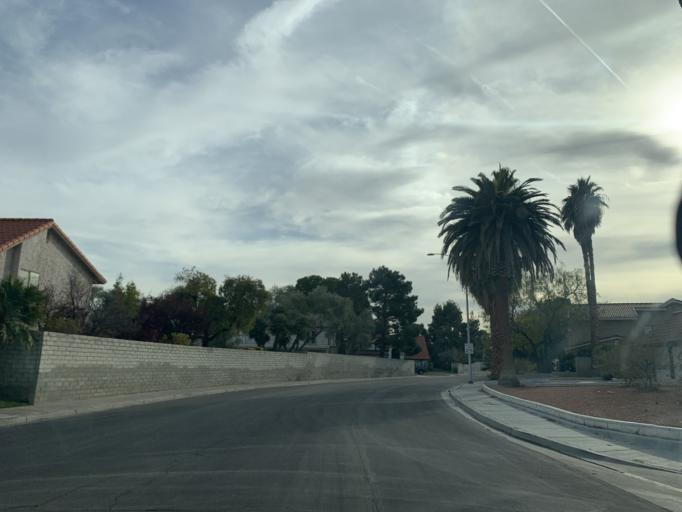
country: US
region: Nevada
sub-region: Clark County
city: Las Vegas
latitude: 36.1511
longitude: -115.1752
